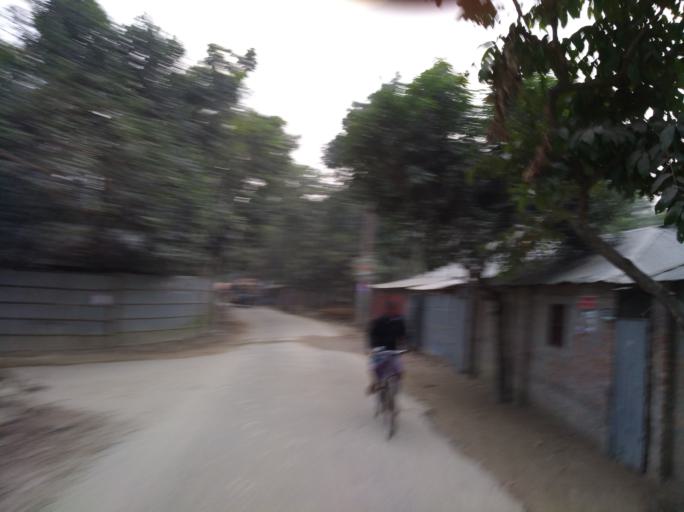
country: BD
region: Rajshahi
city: Saidpur
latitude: 25.9265
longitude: 88.8667
